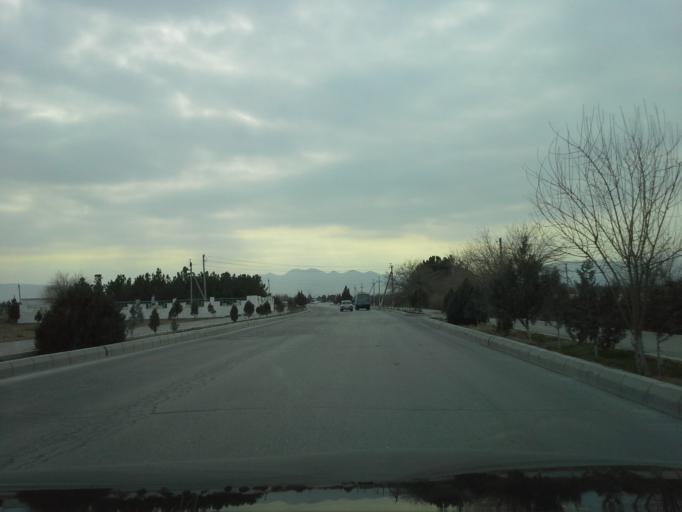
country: TM
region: Ahal
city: Abadan
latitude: 38.0291
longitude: 58.2464
